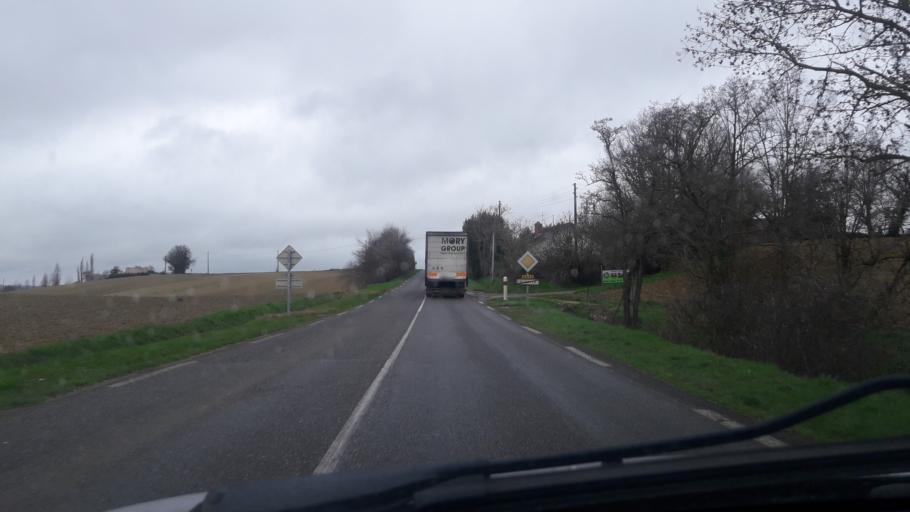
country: FR
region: Midi-Pyrenees
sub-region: Departement du Gers
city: Gimont
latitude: 43.7019
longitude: 0.9959
